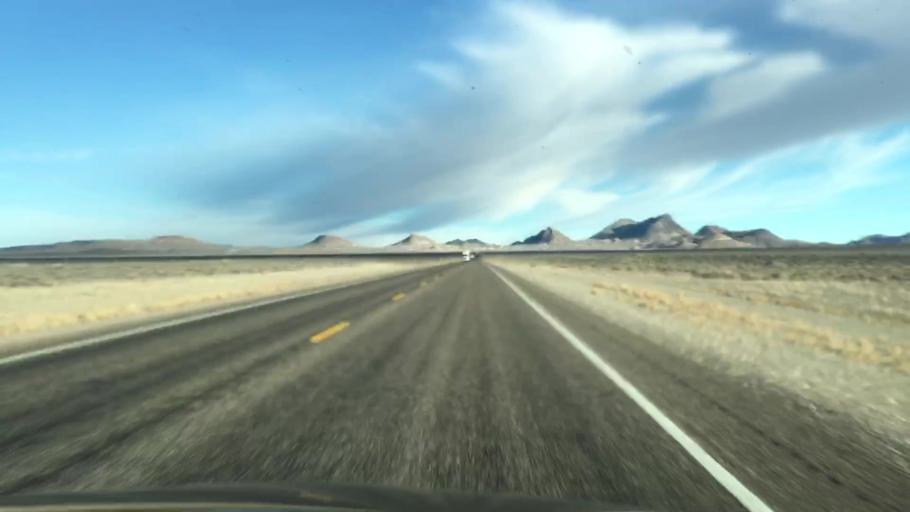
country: US
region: Nevada
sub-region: Nye County
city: Tonopah
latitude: 38.0992
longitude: -117.3259
